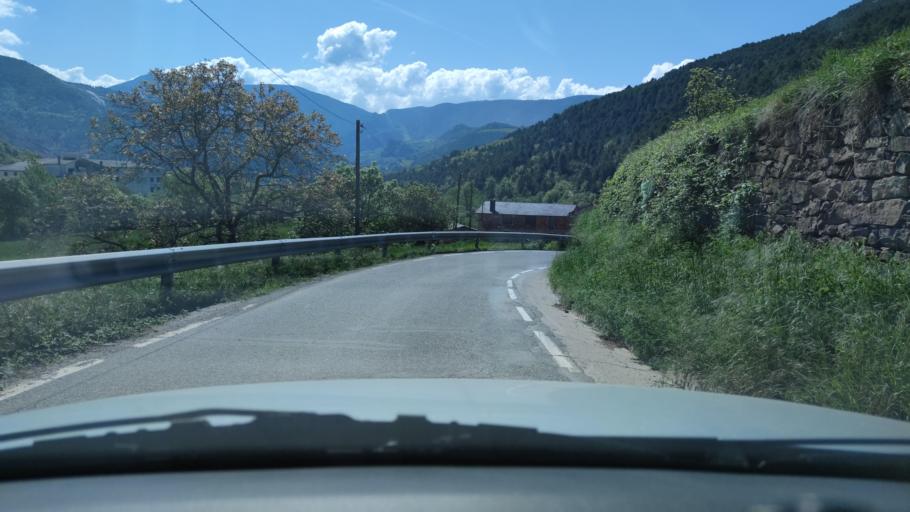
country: ES
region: Catalonia
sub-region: Provincia de Lleida
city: Coll de Nargo
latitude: 42.2938
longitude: 1.3446
